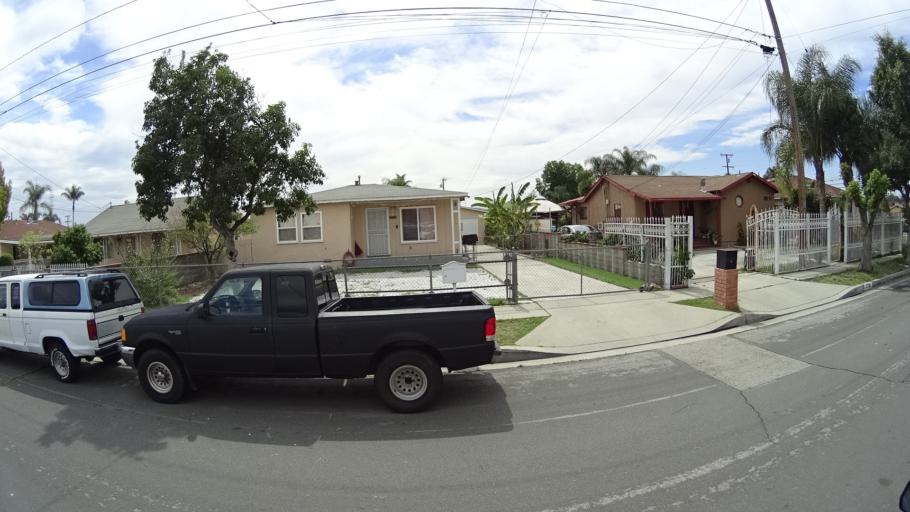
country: US
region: California
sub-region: Los Angeles County
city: El Monte
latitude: 34.0734
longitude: -117.9966
